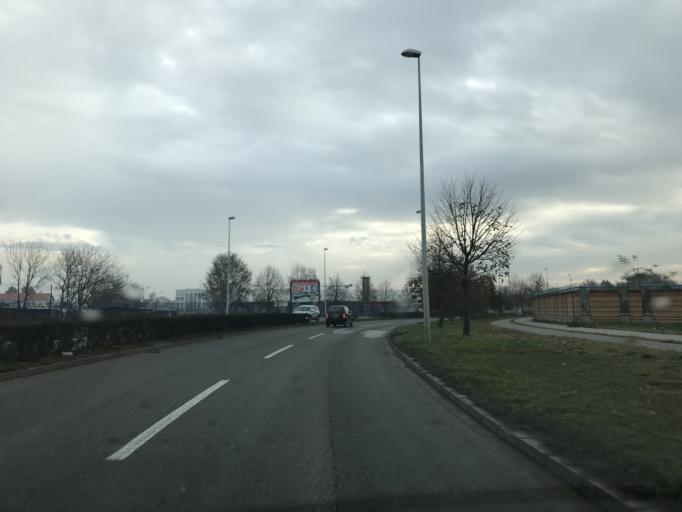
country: RS
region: Autonomna Pokrajina Vojvodina
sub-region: Juznobacki Okrug
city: Novi Sad
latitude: 45.2700
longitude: 19.8277
